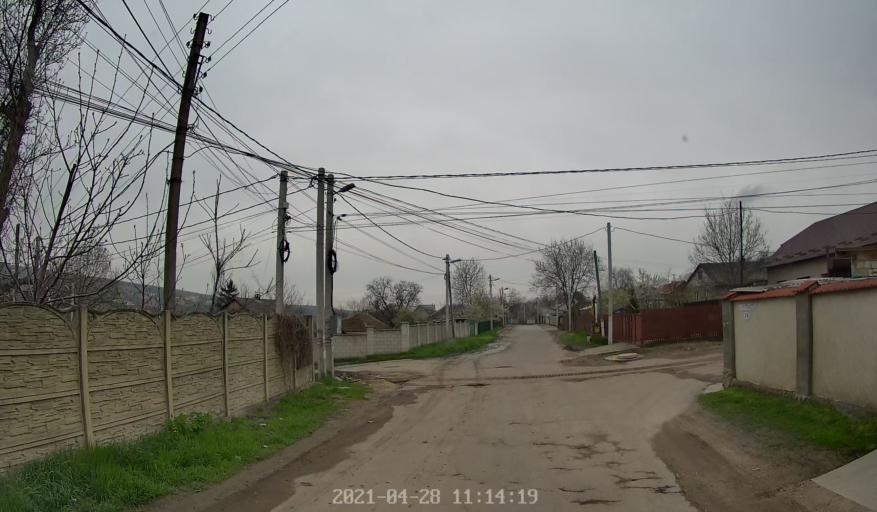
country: MD
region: Chisinau
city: Singera
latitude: 46.9810
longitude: 28.9374
